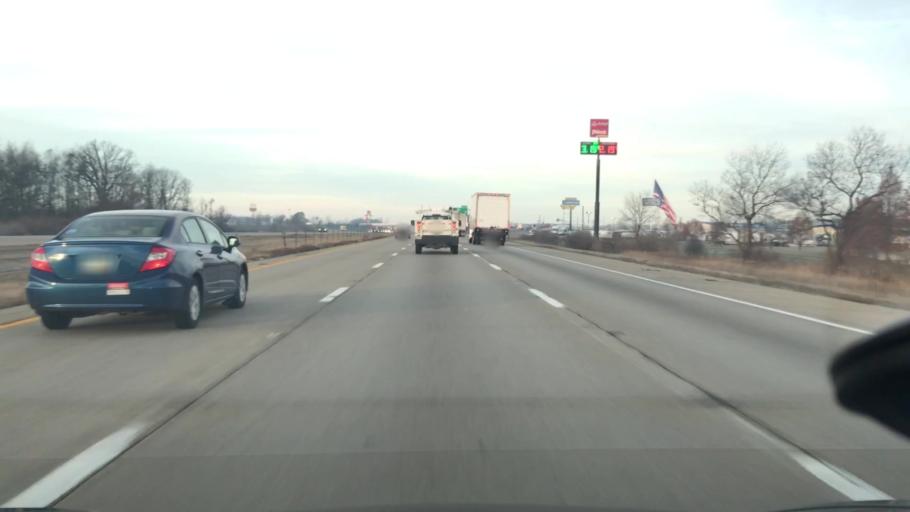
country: US
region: Ohio
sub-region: Madison County
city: West Jefferson
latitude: 39.9573
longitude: -83.3659
